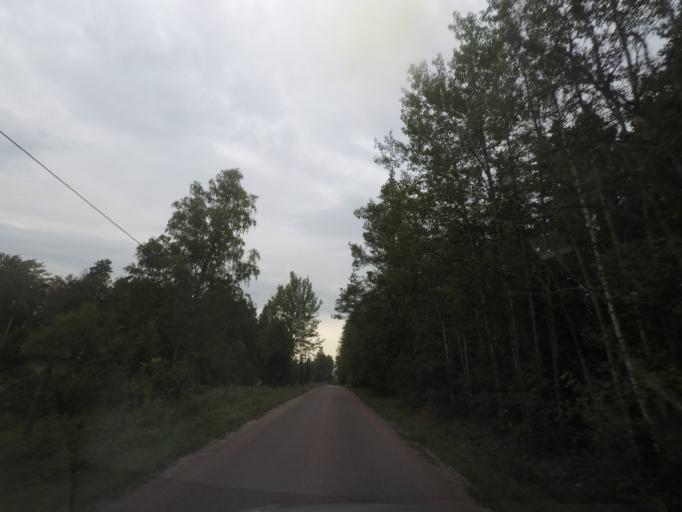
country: SE
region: Vaestmanland
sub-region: Hallstahammars Kommun
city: Kolback
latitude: 59.4939
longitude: 16.1912
